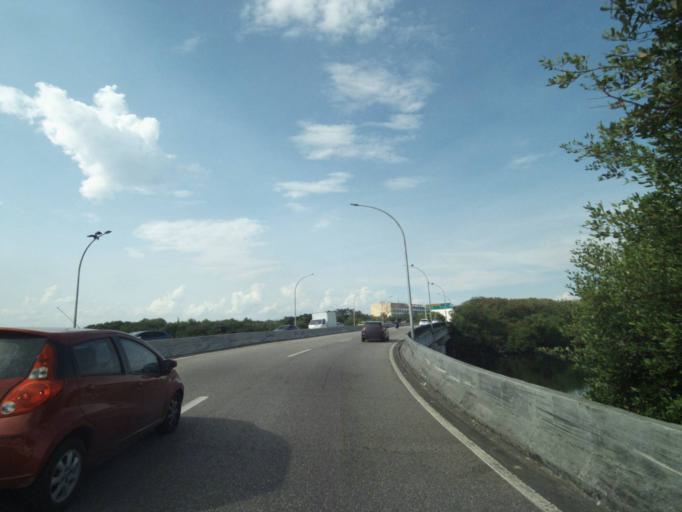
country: BR
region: Rio de Janeiro
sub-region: Rio De Janeiro
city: Rio de Janeiro
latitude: -22.8636
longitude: -43.2339
